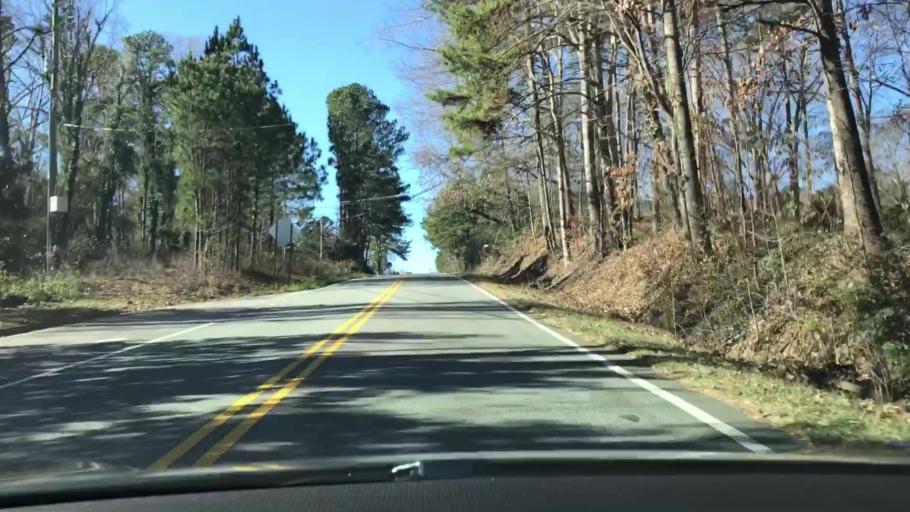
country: US
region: Georgia
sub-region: Forsyth County
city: Cumming
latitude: 34.1835
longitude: -84.1020
